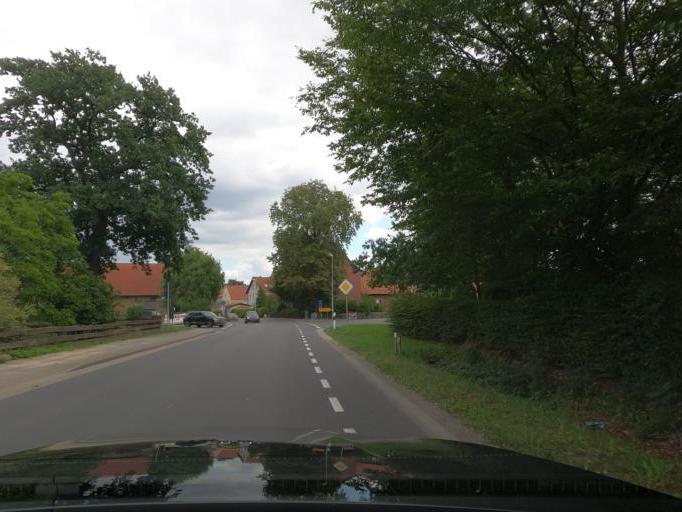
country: DE
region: Lower Saxony
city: Hohenhameln
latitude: 52.3074
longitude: 10.0434
